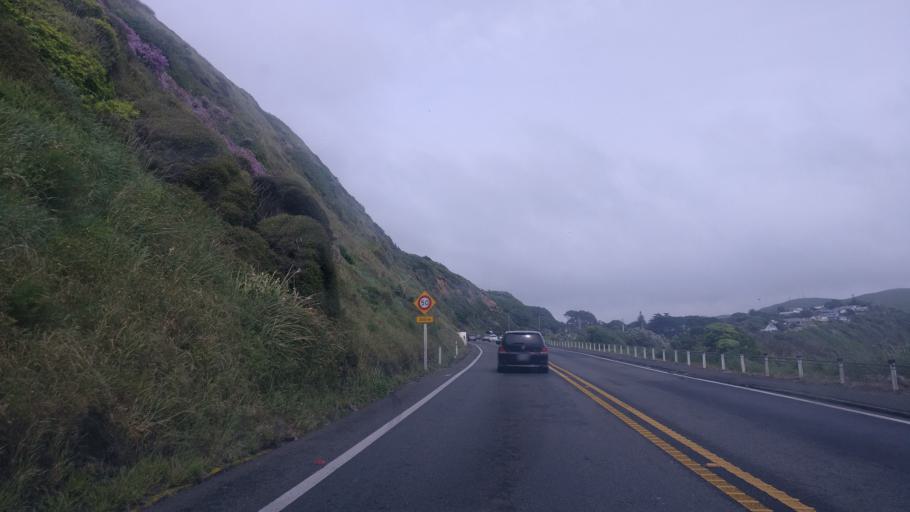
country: NZ
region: Wellington
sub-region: Porirua City
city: Porirua
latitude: -41.0274
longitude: 174.9009
